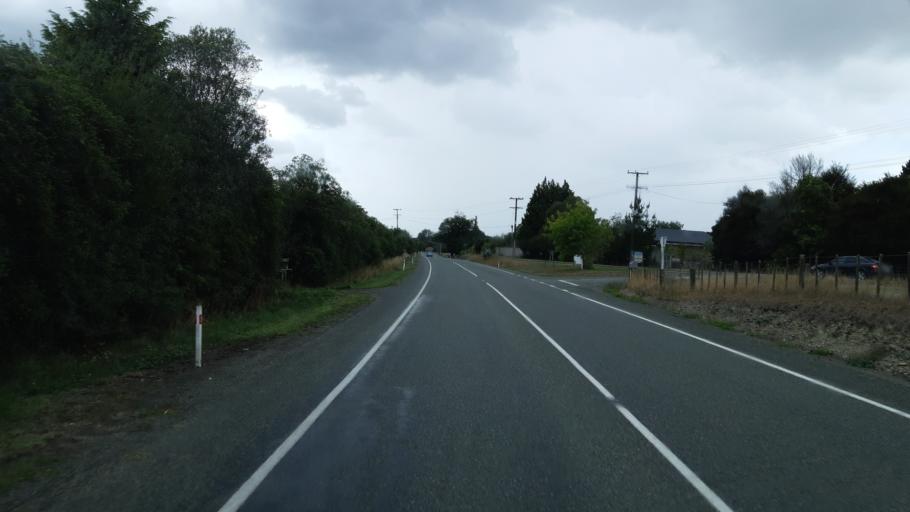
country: NZ
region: Tasman
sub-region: Tasman District
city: Wakefield
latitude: -41.4102
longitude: 173.0241
